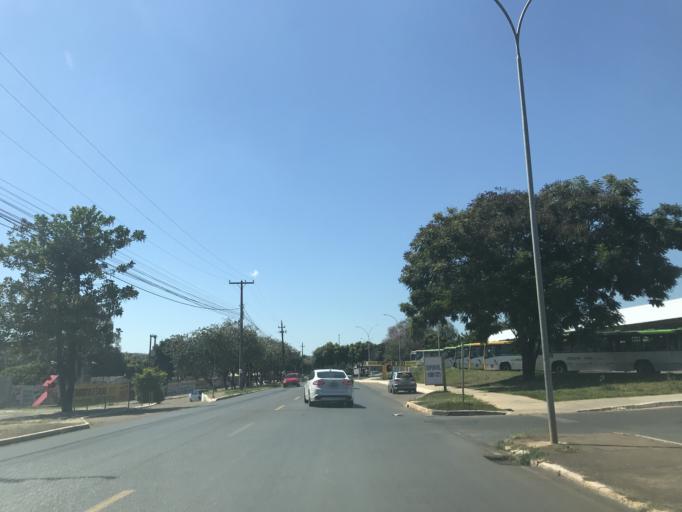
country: BR
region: Federal District
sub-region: Brasilia
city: Brasilia
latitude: -15.6498
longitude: -47.7871
